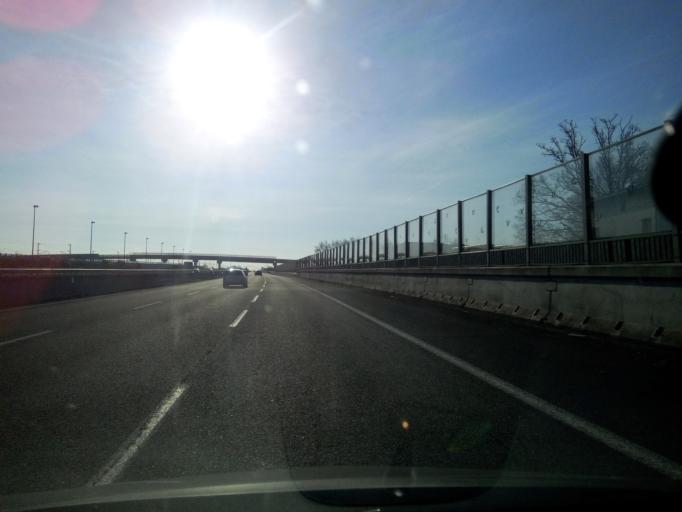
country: IT
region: Emilia-Romagna
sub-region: Provincia di Reggio Emilia
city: Roncocesi
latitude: 44.7414
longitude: 10.5770
